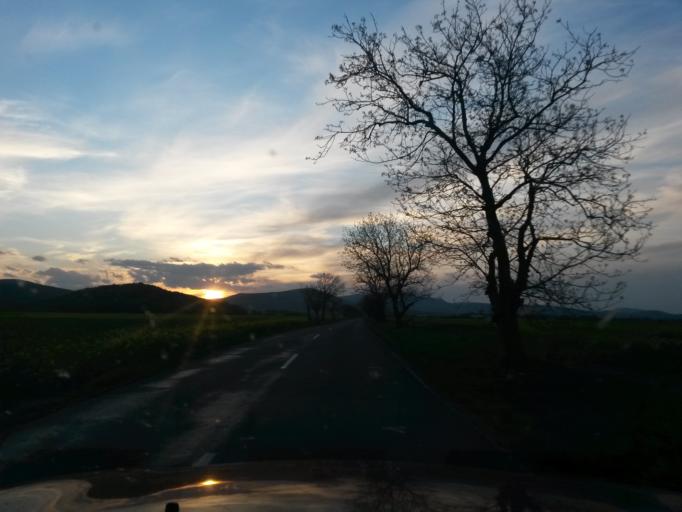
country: HU
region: Borsod-Abauj-Zemplen
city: Satoraljaujhely
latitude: 48.5139
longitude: 21.6059
